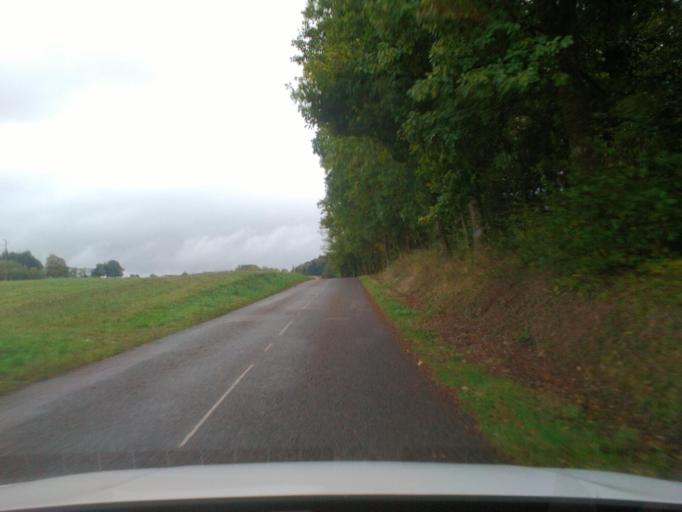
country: FR
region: Lorraine
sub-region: Departement des Vosges
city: Senones
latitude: 48.3668
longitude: 6.9641
